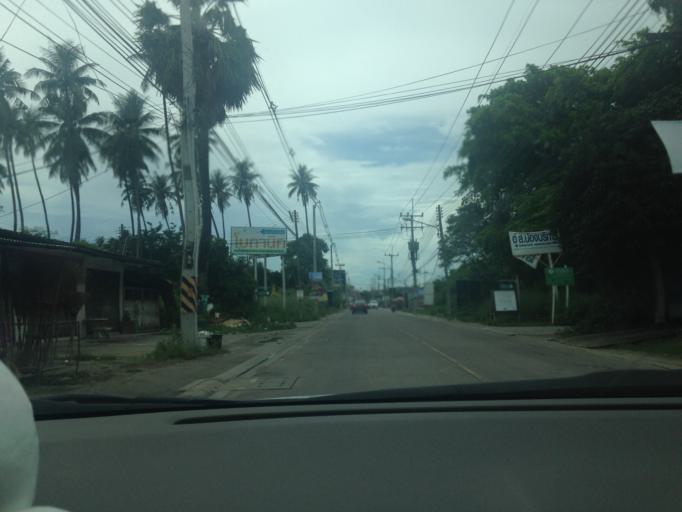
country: TH
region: Chon Buri
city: Chon Buri
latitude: 13.3193
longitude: 100.9295
